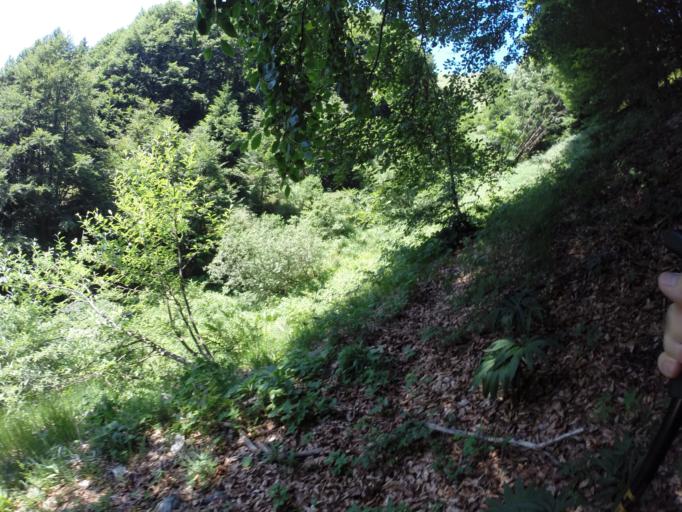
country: IT
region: Veneto
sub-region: Provincia di Treviso
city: Crespano del Grappa
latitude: 45.9047
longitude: 11.8281
